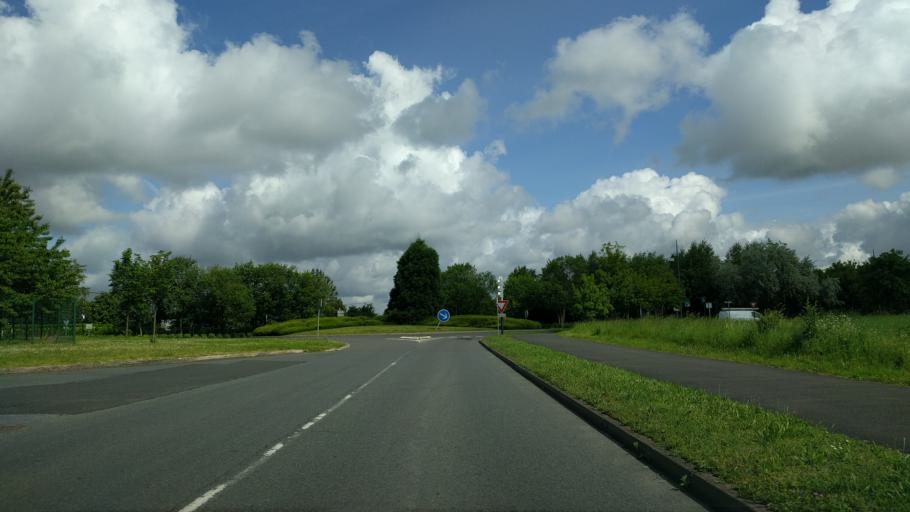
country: FR
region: Ile-de-France
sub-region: Departement de Seine-et-Marne
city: Savigny-le-Temple
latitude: 48.5787
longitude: 2.5947
